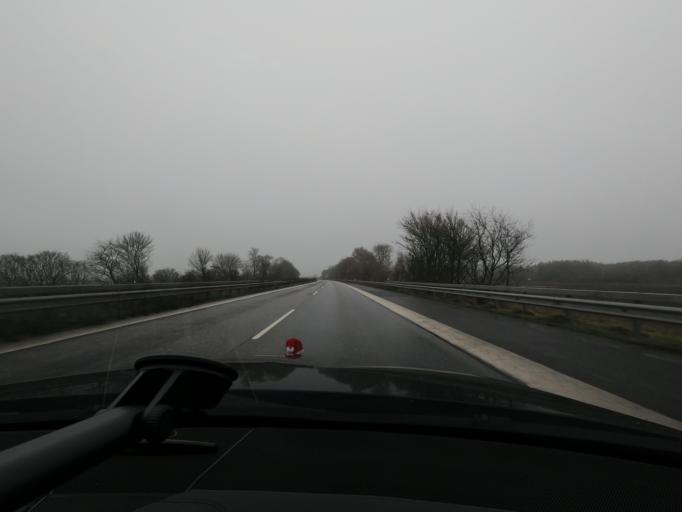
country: DE
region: Schleswig-Holstein
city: Brekendorf
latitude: 54.4202
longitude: 9.6052
